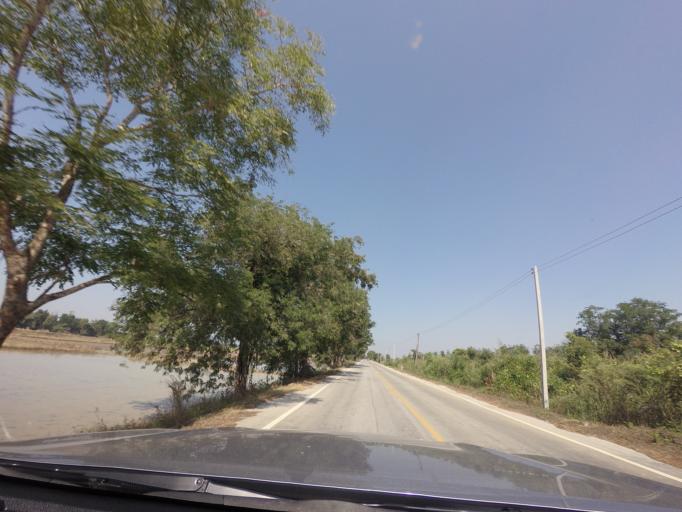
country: TH
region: Sukhothai
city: Sukhothai
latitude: 17.0834
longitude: 99.7907
